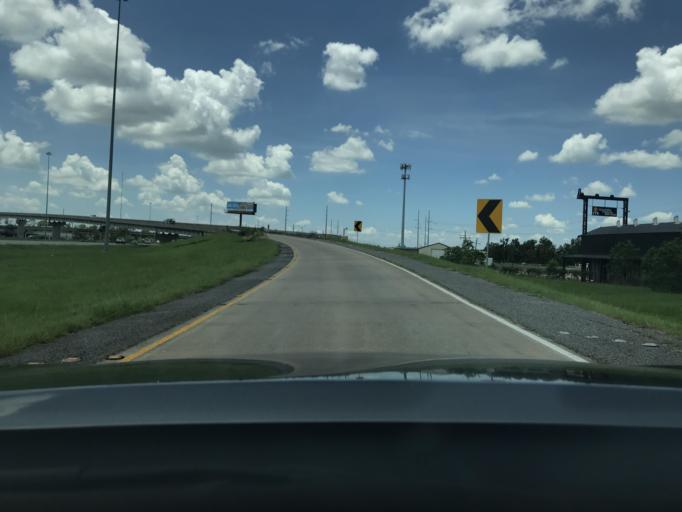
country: US
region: Louisiana
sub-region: Calcasieu Parish
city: Westlake
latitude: 30.2303
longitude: -93.2979
